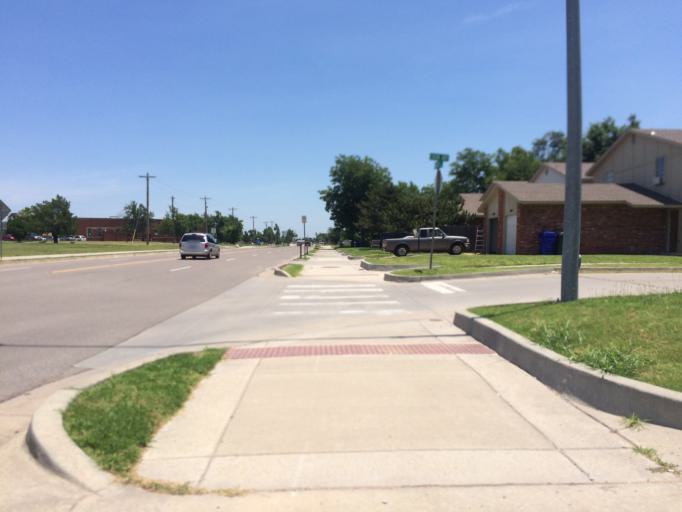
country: US
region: Oklahoma
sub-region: Cleveland County
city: Norman
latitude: 35.2256
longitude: -97.4308
